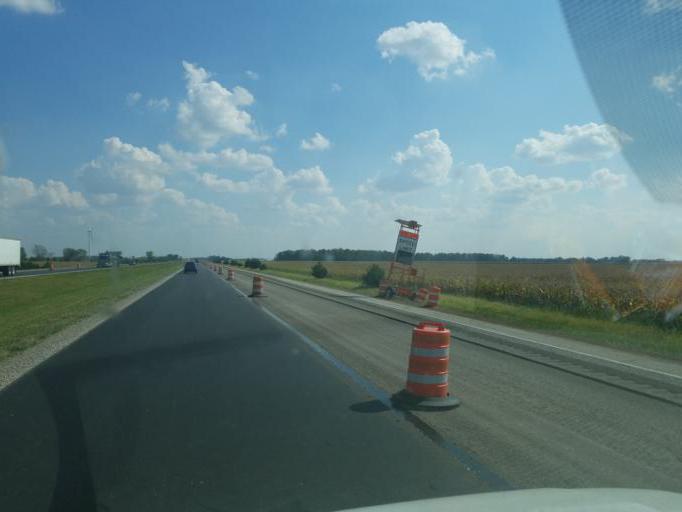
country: US
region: Ohio
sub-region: Van Wert County
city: Convoy
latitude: 40.9229
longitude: -84.6814
